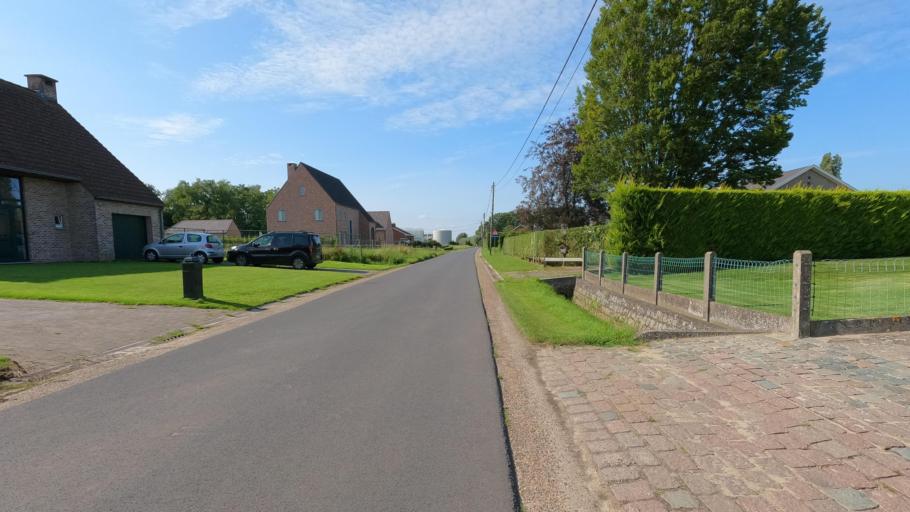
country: BE
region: Flanders
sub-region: Provincie Antwerpen
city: Berlaar
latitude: 51.0994
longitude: 4.6652
